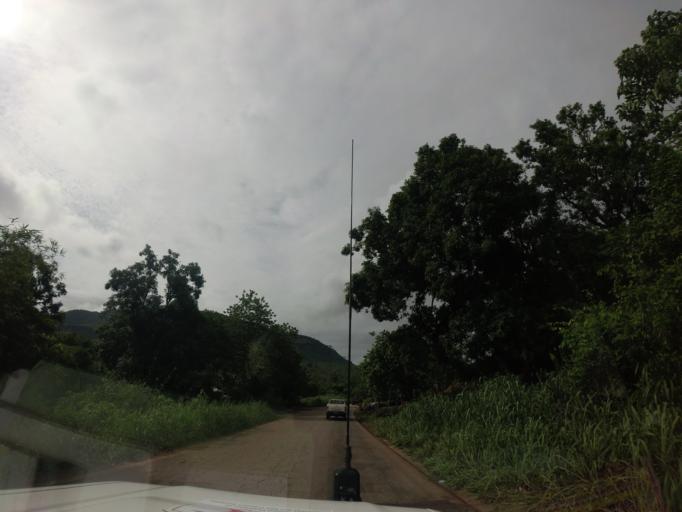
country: GN
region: Kindia
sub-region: Coyah
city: Coyah
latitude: 9.7288
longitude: -13.3713
